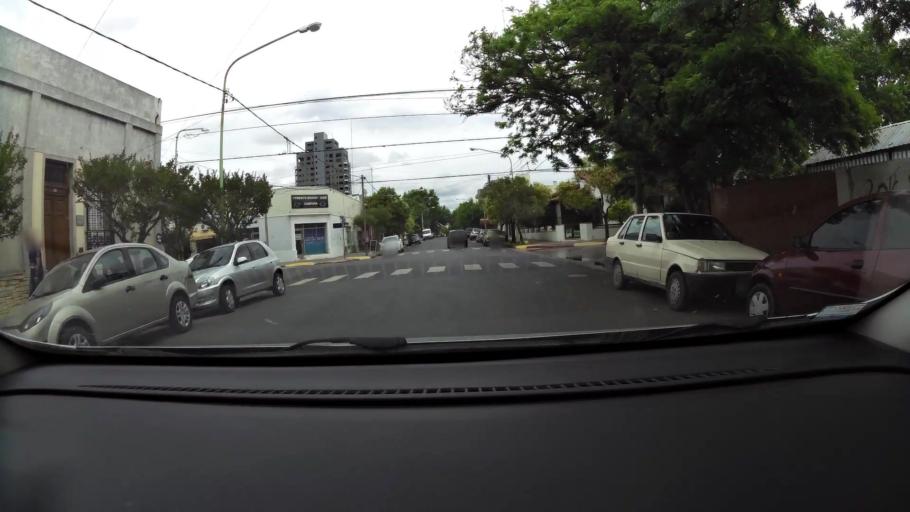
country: AR
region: Buenos Aires
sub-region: Partido de Campana
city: Campana
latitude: -34.1619
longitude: -58.9613
